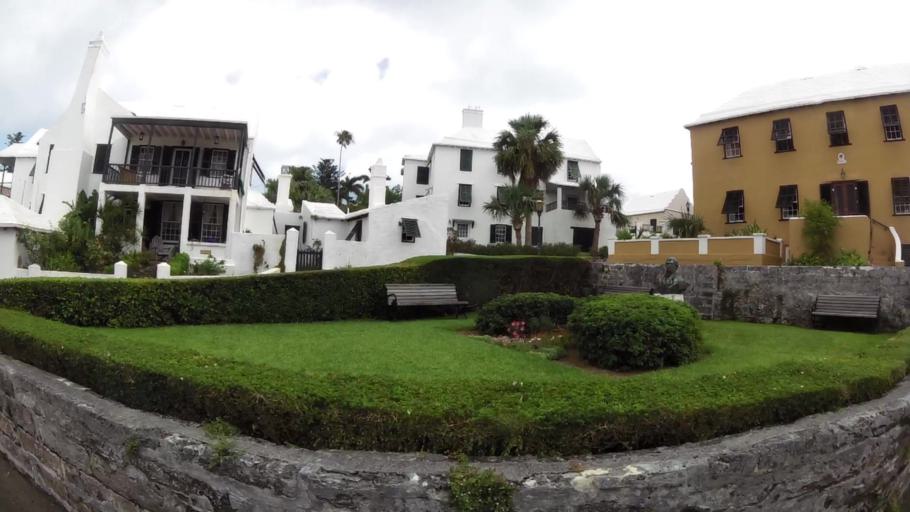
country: BM
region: Saint George
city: Saint George
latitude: 32.3813
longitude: -64.6762
